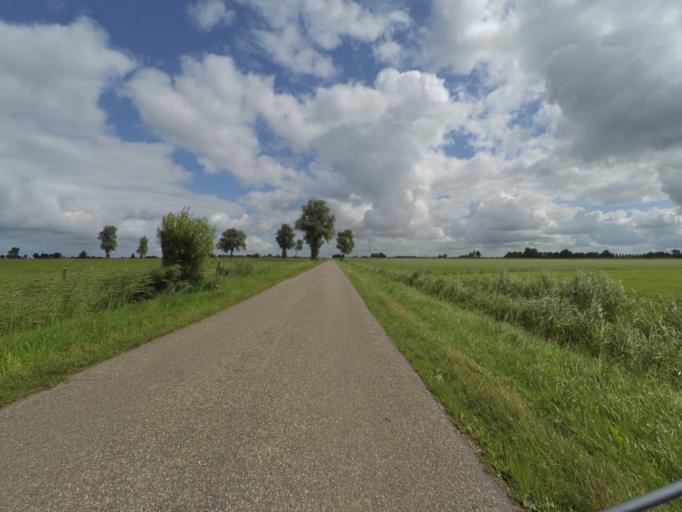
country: NL
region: Friesland
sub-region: Gemeente Kollumerland en Nieuwkruisland
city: Kollum
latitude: 53.2710
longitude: 6.1776
